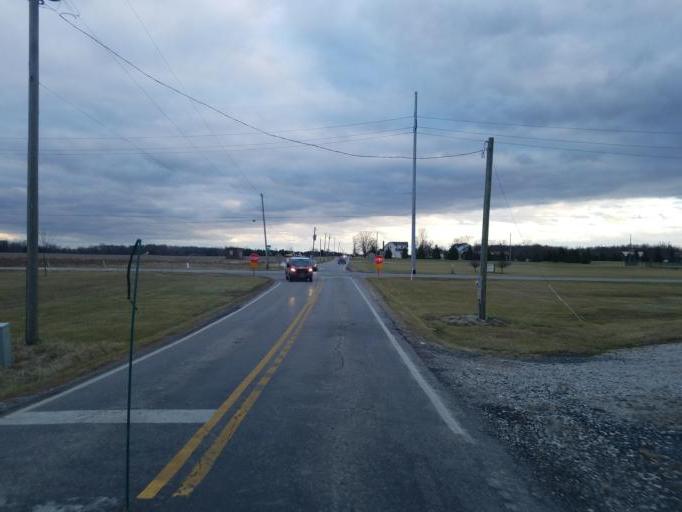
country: US
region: Ohio
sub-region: Delaware County
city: Delaware
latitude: 40.3334
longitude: -83.1006
